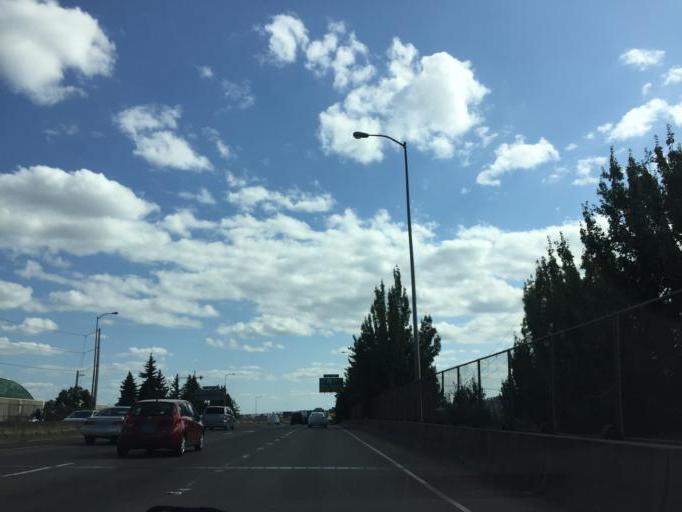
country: US
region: Oregon
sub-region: Multnomah County
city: Portland
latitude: 45.5310
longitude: -122.6654
